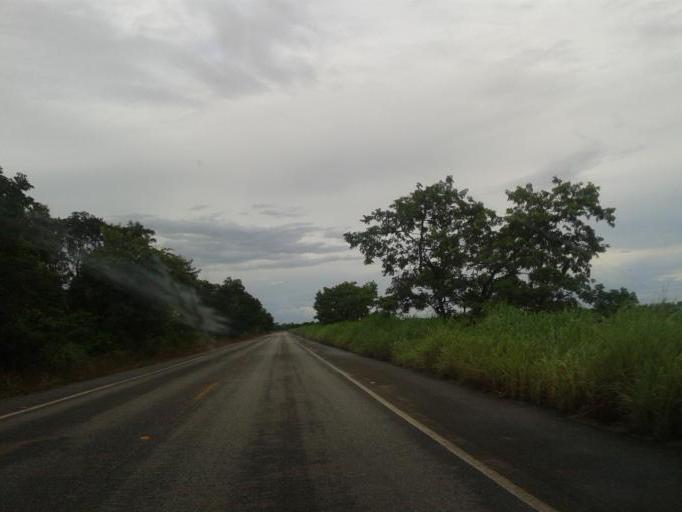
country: BR
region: Goias
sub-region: Mozarlandia
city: Mozarlandia
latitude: -14.8505
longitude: -50.5442
